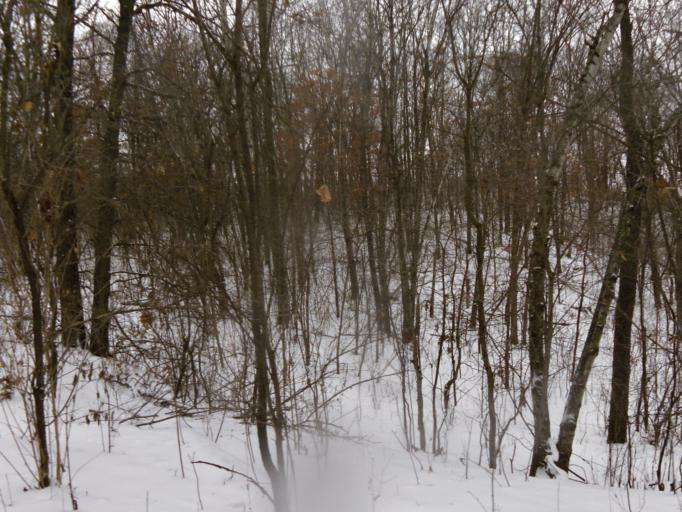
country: US
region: Minnesota
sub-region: Dakota County
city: Inver Grove Heights
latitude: 44.8556
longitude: -93.0743
